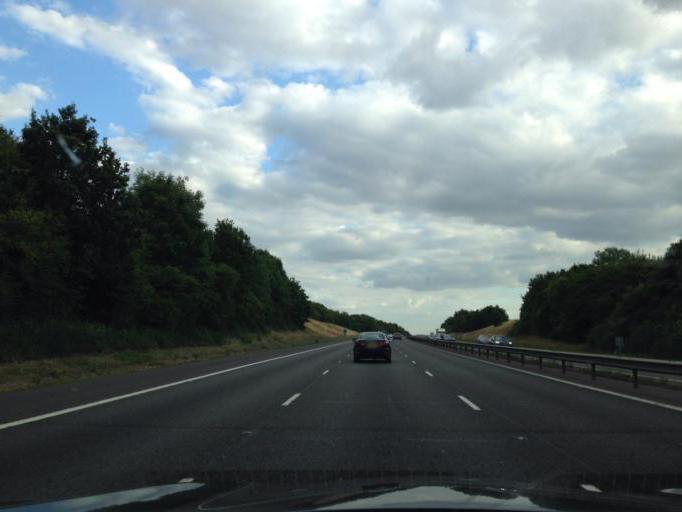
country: GB
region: England
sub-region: Oxfordshire
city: Somerton
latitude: 51.9986
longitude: -1.2691
